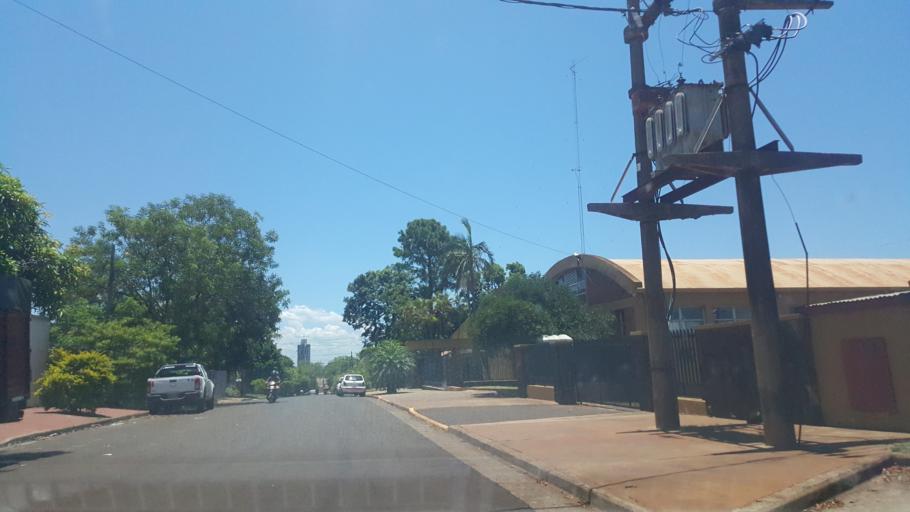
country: AR
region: Misiones
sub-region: Departamento de Capital
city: Posadas
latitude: -27.3822
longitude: -55.8871
